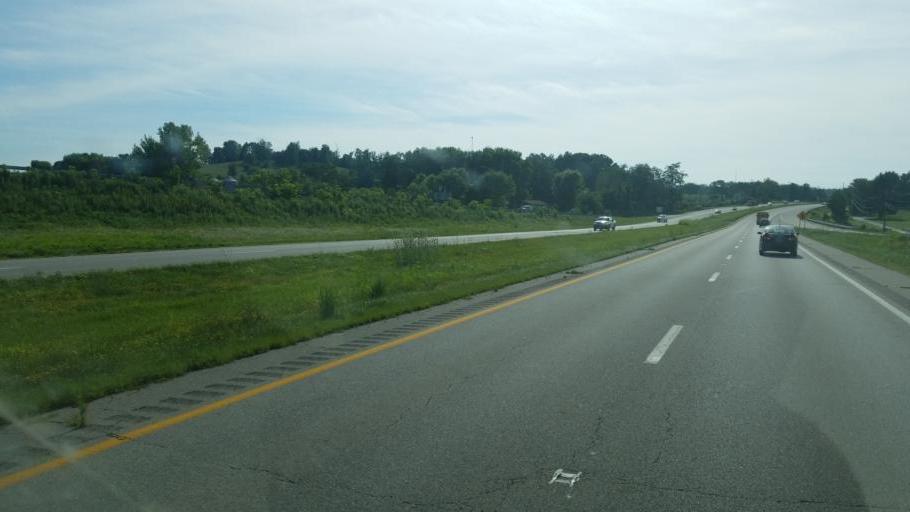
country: US
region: Ohio
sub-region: Hocking County
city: Logan
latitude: 39.5595
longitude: -82.4962
